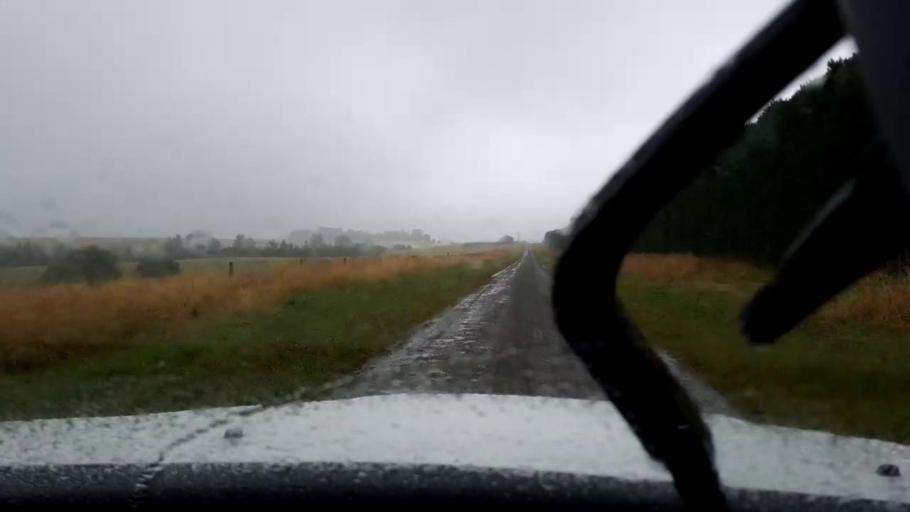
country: NZ
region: Canterbury
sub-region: Timaru District
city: Pleasant Point
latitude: -44.1695
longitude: 171.1507
